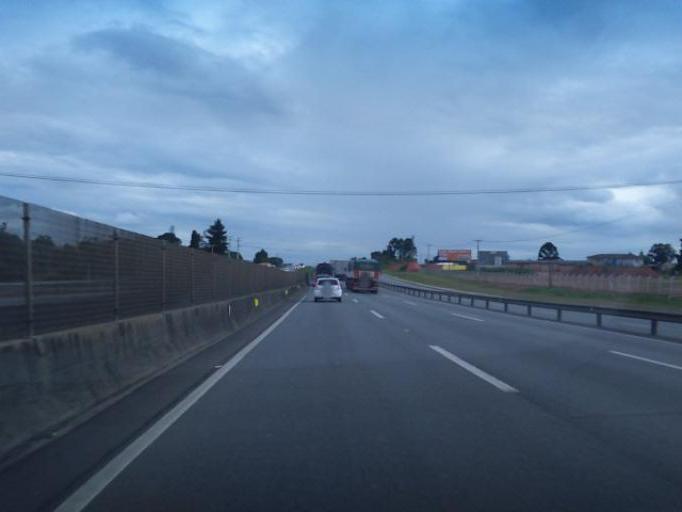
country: BR
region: Parana
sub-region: Sao Jose Dos Pinhais
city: Sao Jose dos Pinhais
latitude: -25.6172
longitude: -49.1693
